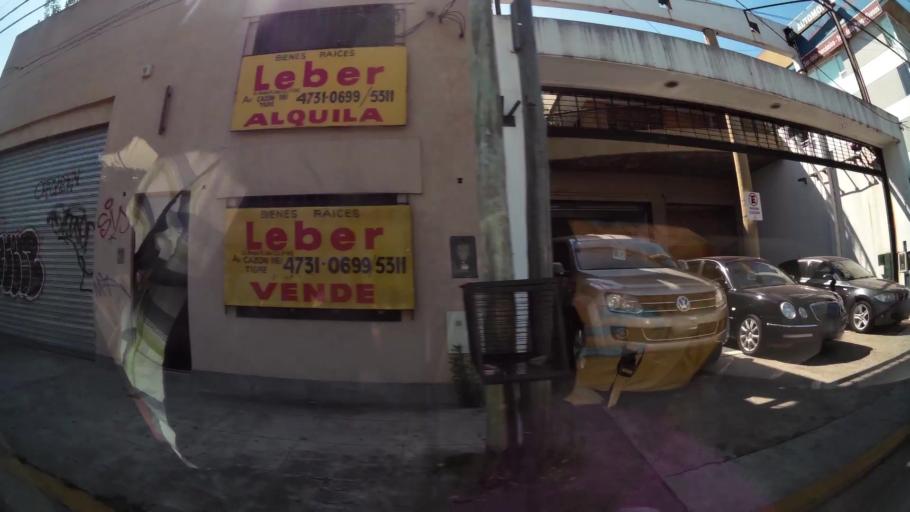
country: AR
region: Buenos Aires
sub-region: Partido de Tigre
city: Tigre
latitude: -34.4287
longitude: -58.5838
